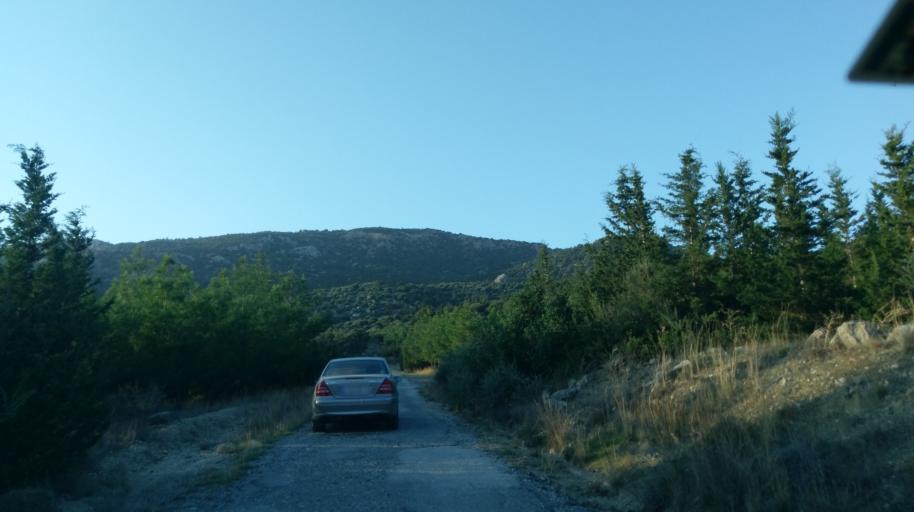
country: CY
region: Ammochostos
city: Trikomo
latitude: 35.3721
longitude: 33.9019
